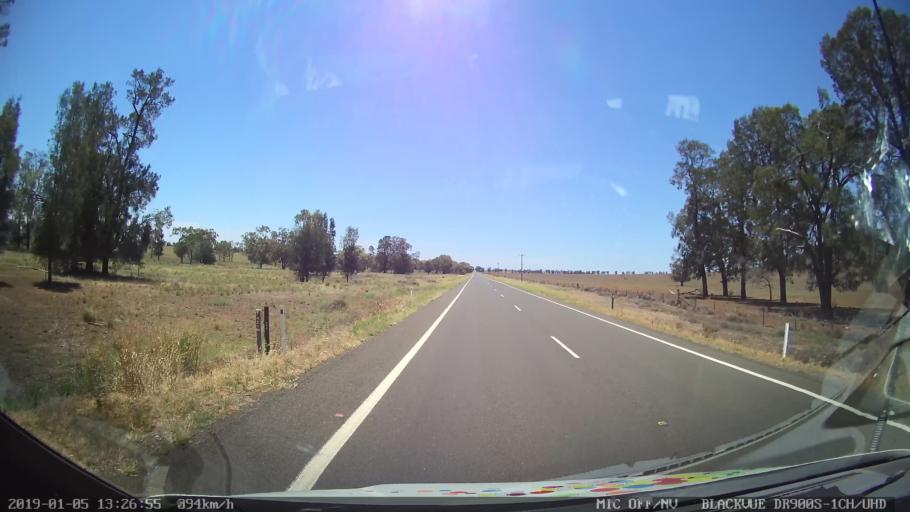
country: AU
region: New South Wales
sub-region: Gunnedah
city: Gunnedah
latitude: -31.0490
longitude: 150.0222
